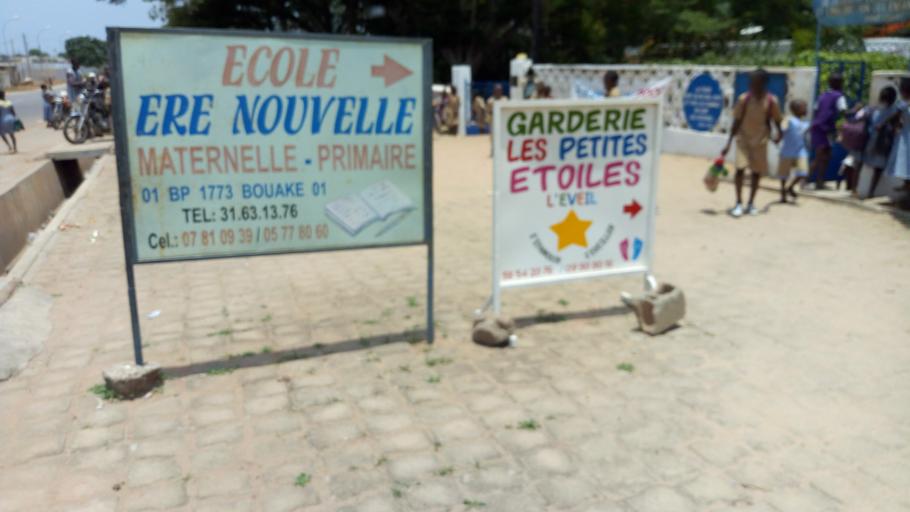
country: CI
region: Vallee du Bandama
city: Bouake
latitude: 7.6738
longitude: -5.0161
